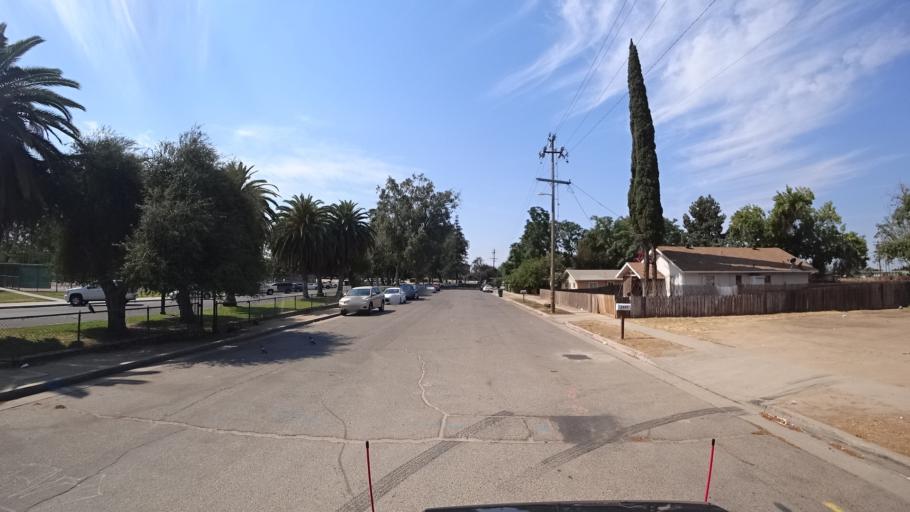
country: US
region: California
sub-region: Fresno County
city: West Park
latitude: 36.7566
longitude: -119.8267
